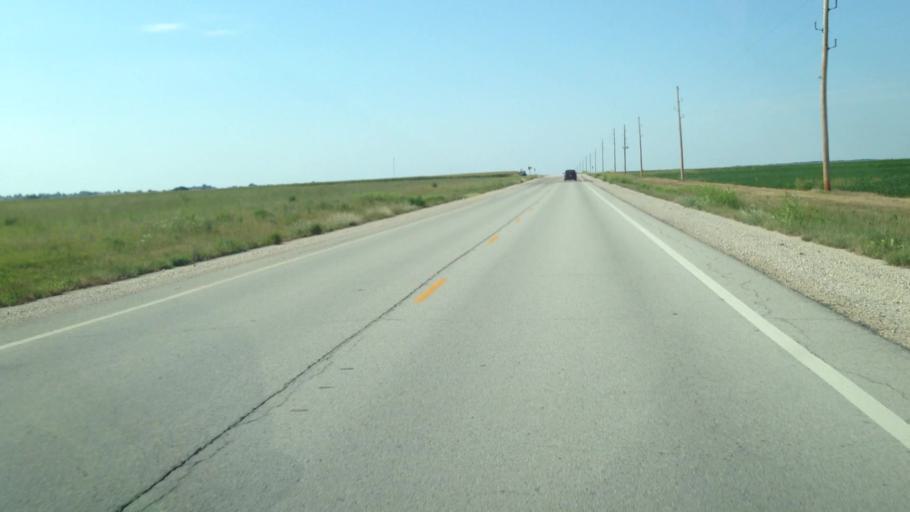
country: US
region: Kansas
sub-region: Anderson County
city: Garnett
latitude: 38.0492
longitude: -95.1695
